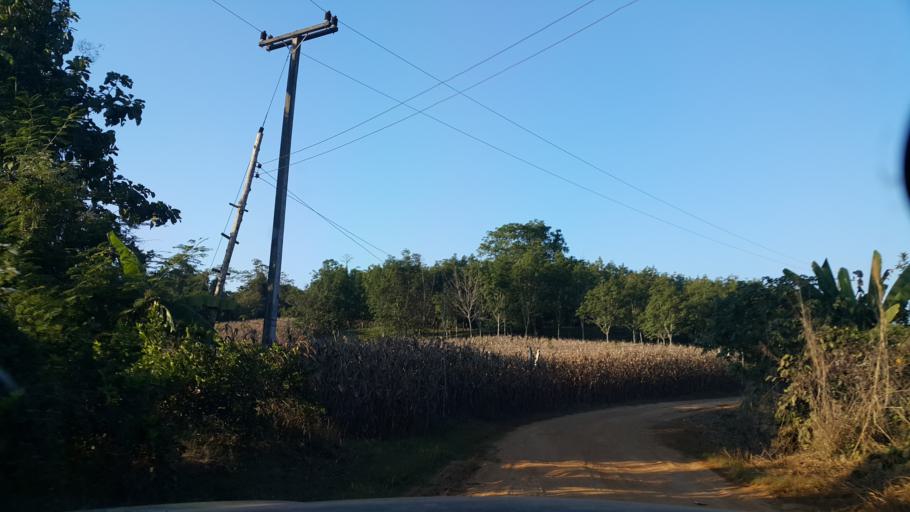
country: TH
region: Sukhothai
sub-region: Amphoe Si Satchanalai
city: Si Satchanalai
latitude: 17.6037
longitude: 99.6145
